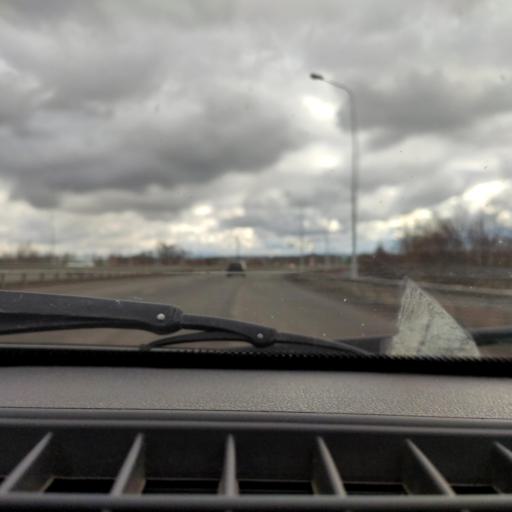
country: RU
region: Bashkortostan
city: Ufa
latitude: 54.6626
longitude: 56.0774
